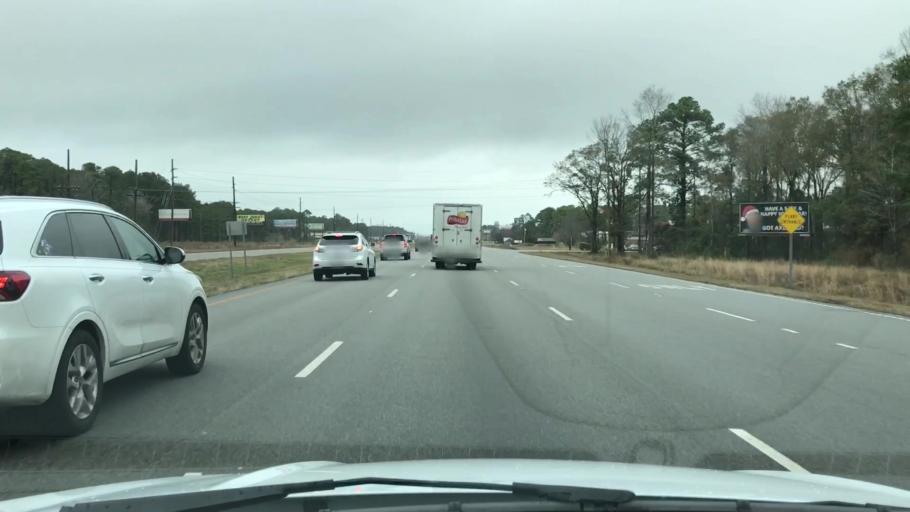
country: US
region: South Carolina
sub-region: Horry County
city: Forestbrook
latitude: 33.7708
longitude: -78.9787
